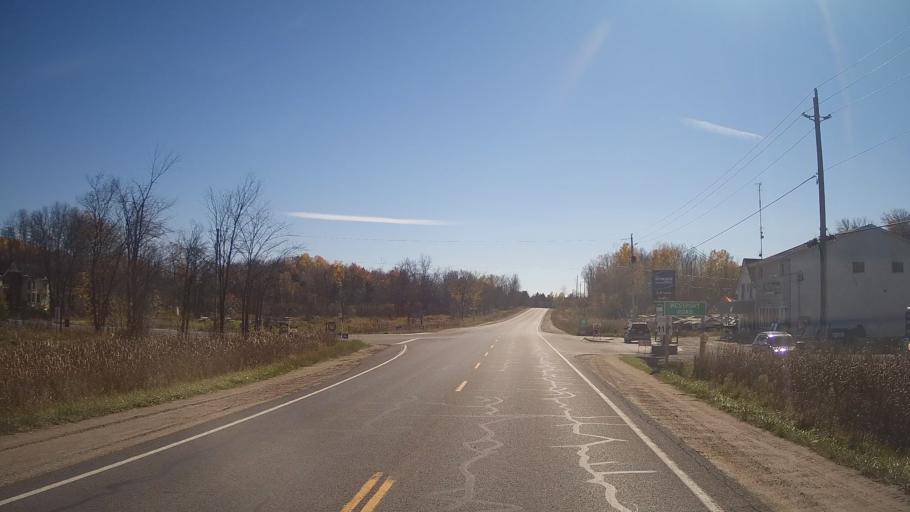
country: CA
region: Ontario
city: Kingston
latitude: 44.5436
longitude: -76.6790
